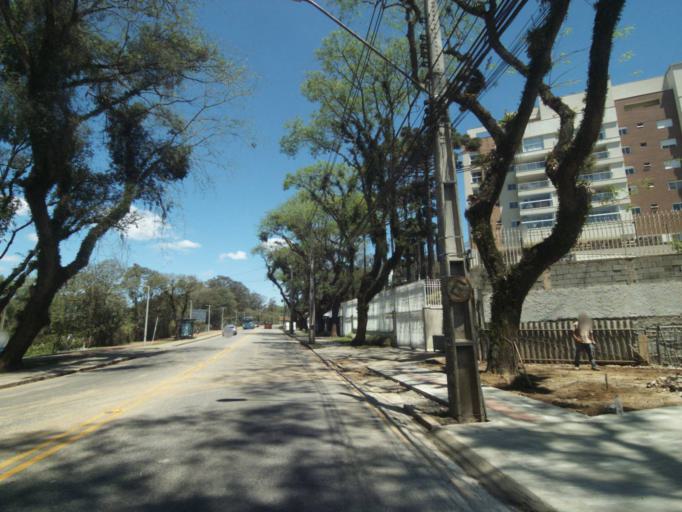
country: BR
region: Parana
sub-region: Curitiba
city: Curitiba
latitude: -25.3926
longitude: -49.2694
